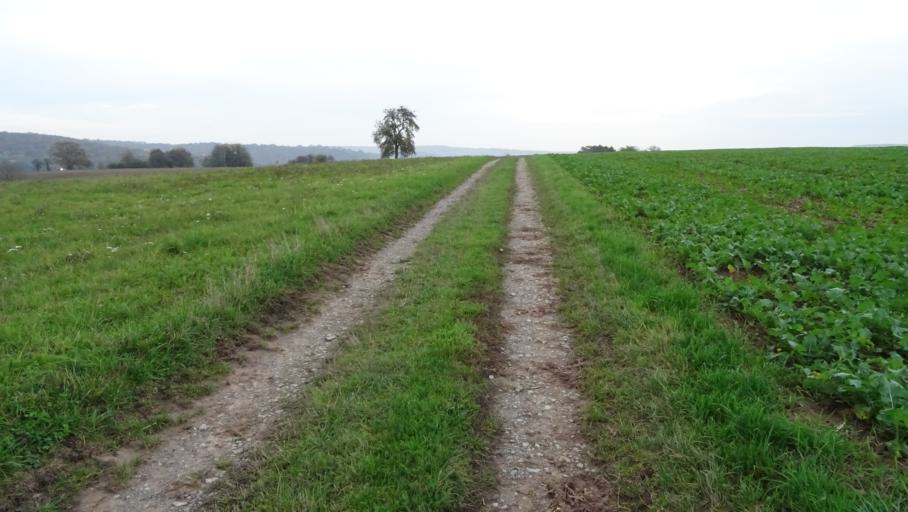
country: DE
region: Baden-Wuerttemberg
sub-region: Karlsruhe Region
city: Binau
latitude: 49.3765
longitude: 9.0766
